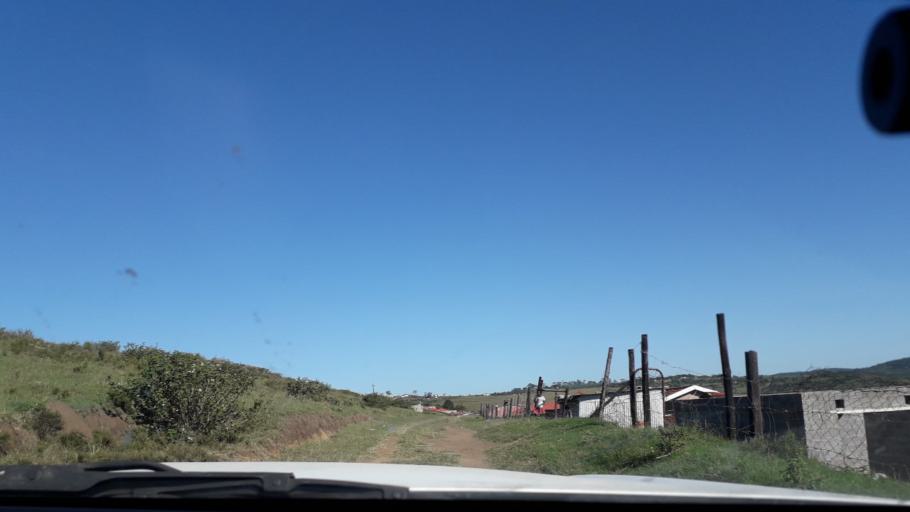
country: ZA
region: Eastern Cape
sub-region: Buffalo City Metropolitan Municipality
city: East London
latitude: -32.8373
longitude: 27.9989
